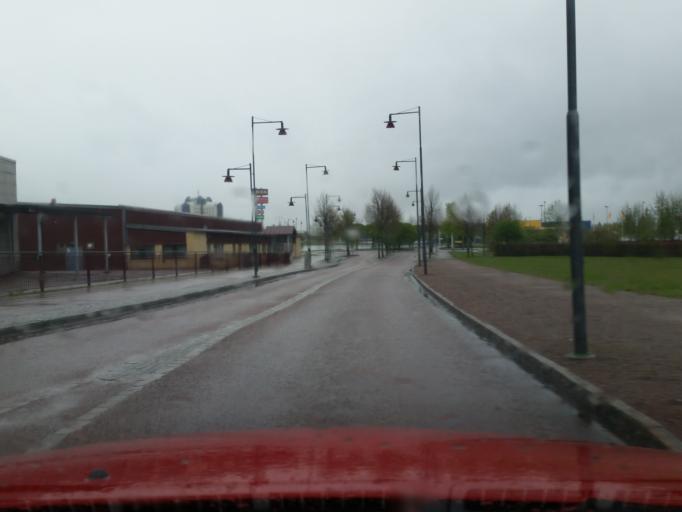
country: SE
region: Dalarna
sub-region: Borlange Kommun
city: Borlaenge
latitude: 60.4827
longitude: 15.4118
